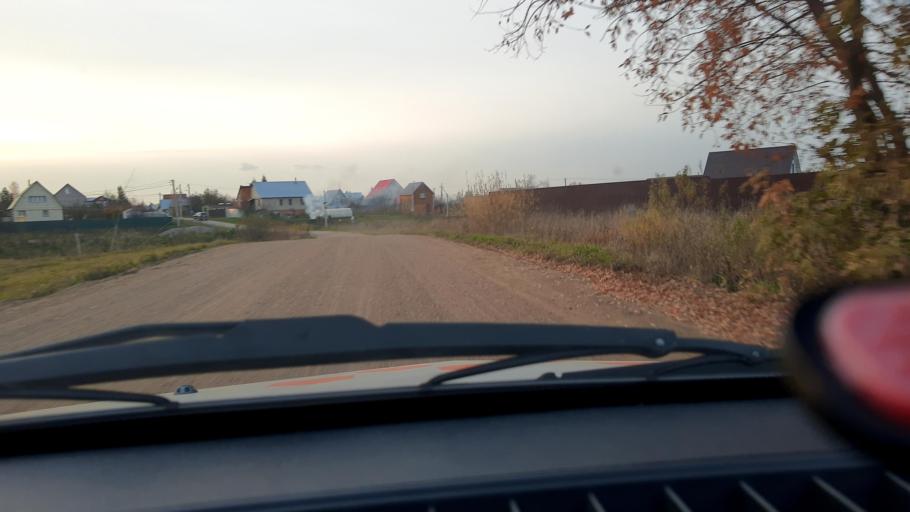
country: RU
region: Bashkortostan
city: Iglino
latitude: 54.7918
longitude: 56.3260
